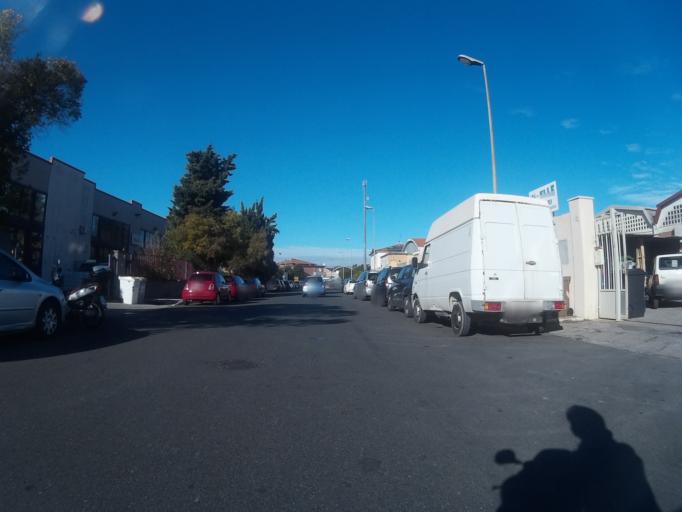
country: IT
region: Tuscany
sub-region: Provincia di Livorno
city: Livorno
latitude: 43.5674
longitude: 10.3374
